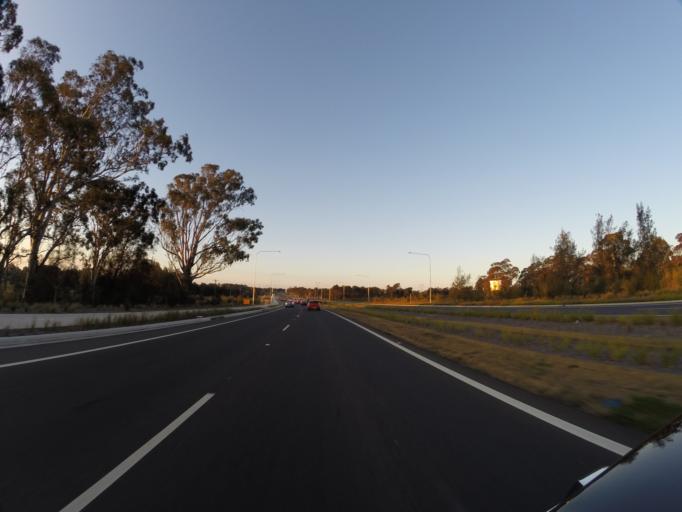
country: AU
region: New South Wales
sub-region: Campbelltown Municipality
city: Denham Court
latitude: -33.9964
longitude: 150.7853
